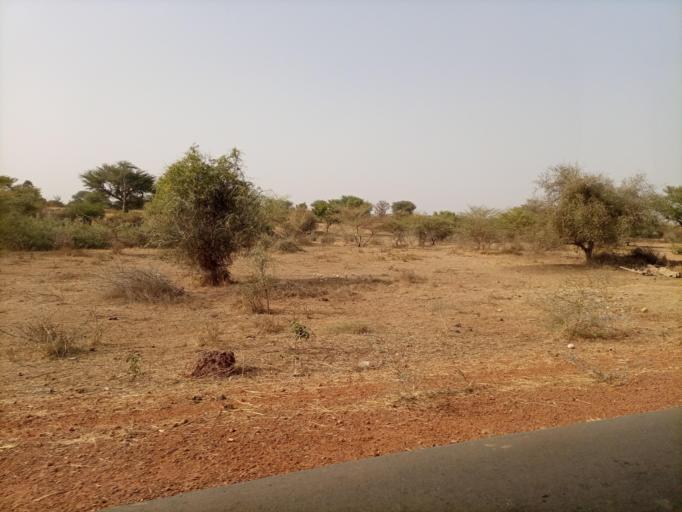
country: SN
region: Fatick
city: Foundiougne
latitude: 14.1240
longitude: -16.4249
